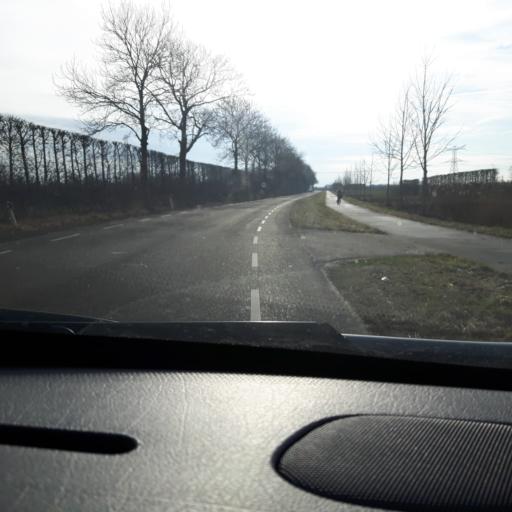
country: NL
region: Zeeland
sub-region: Gemeente Goes
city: Goes
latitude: 51.4433
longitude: 3.9003
